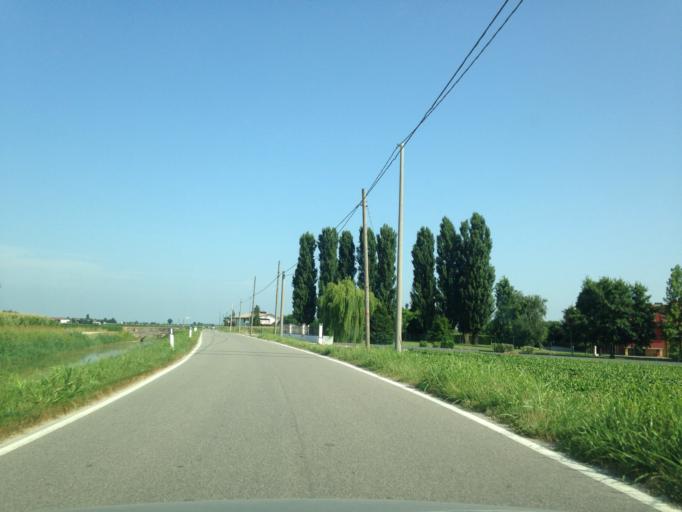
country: IT
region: Veneto
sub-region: Provincia di Venezia
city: Lugugnana
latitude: 45.7239
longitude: 12.9365
